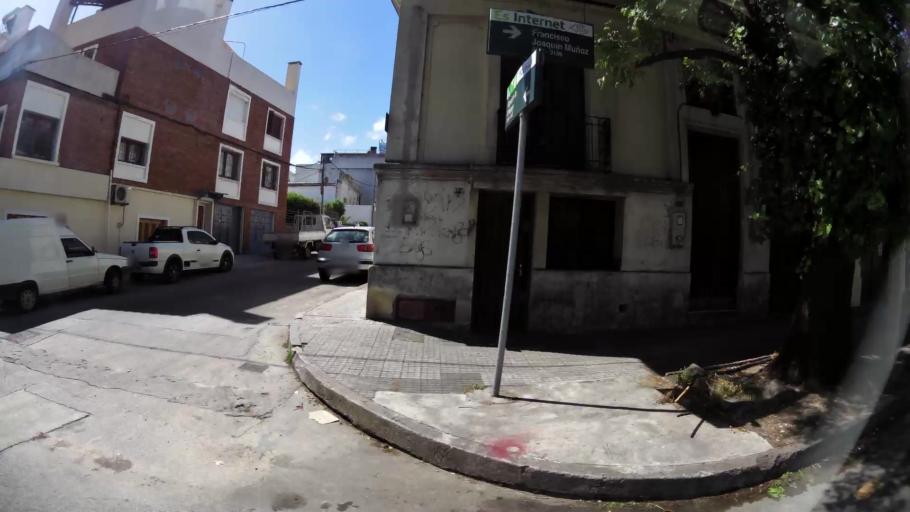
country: UY
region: Montevideo
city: Montevideo
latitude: -34.9051
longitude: -56.1468
